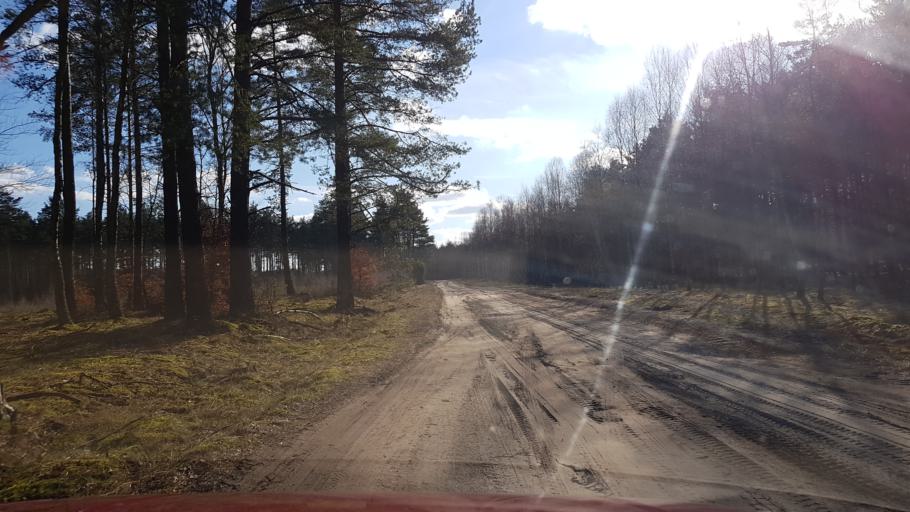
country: PL
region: Greater Poland Voivodeship
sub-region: Powiat zlotowski
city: Sypniewo
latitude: 53.5429
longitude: 16.6480
